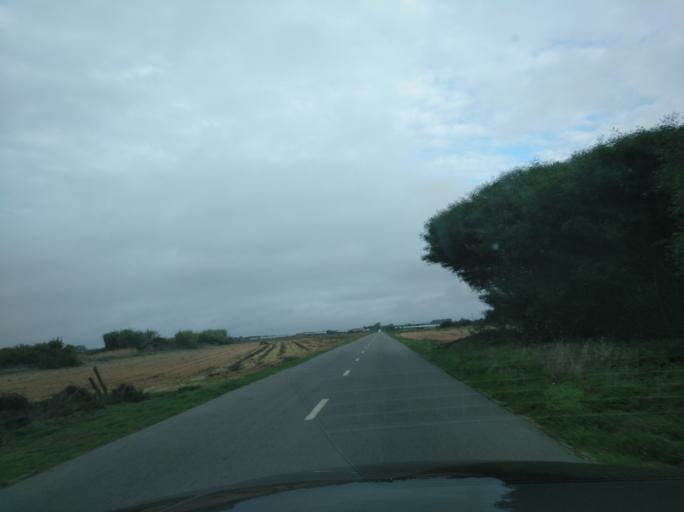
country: PT
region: Beja
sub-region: Odemira
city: Vila Nova de Milfontes
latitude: 37.5993
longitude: -8.8006
